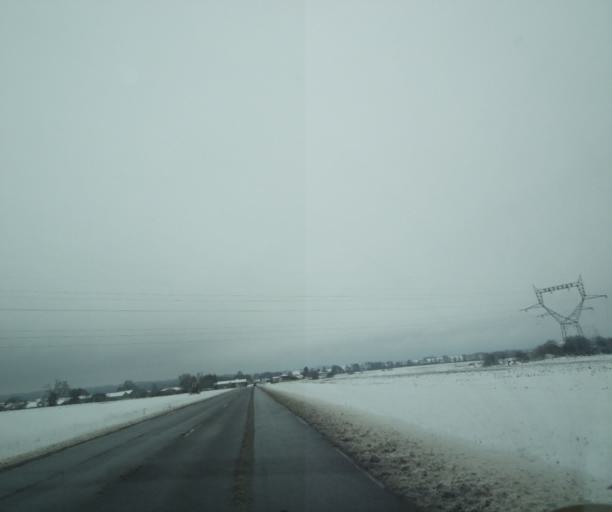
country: FR
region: Champagne-Ardenne
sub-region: Departement de la Haute-Marne
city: Montier-en-Der
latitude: 48.5016
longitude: 4.7880
